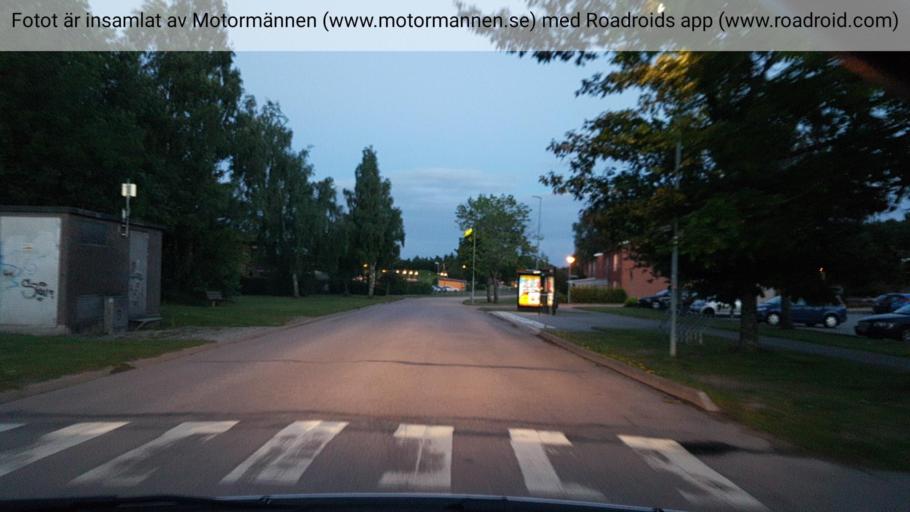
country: SE
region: Vaestmanland
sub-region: Vasteras
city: Vasteras
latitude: 59.6452
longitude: 16.5384
